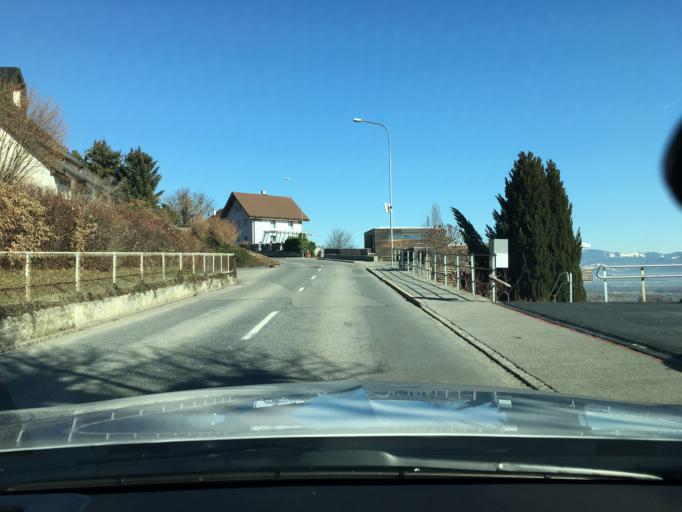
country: CH
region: Saint Gallen
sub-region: Wahlkreis Rheintal
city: Altstatten
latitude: 47.3869
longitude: 9.5474
